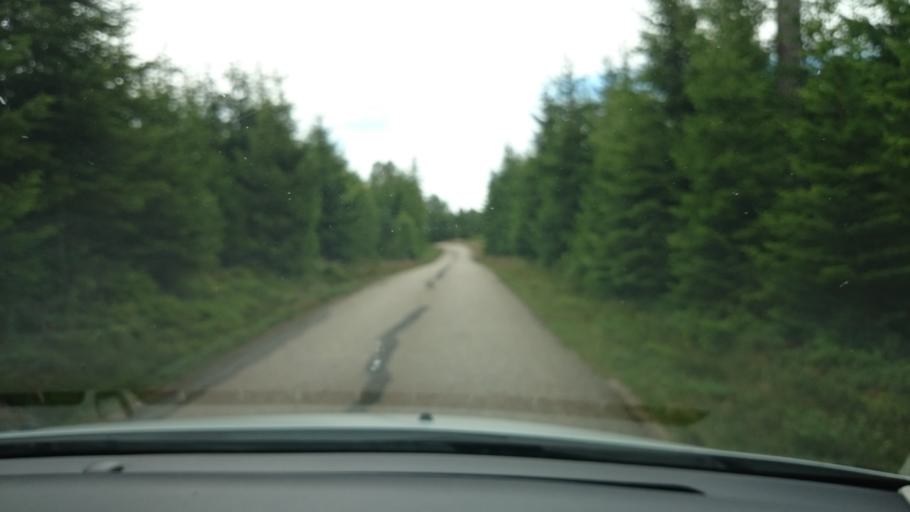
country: SE
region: Halland
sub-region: Hylte Kommun
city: Hyltebruk
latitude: 56.9735
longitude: 13.2027
